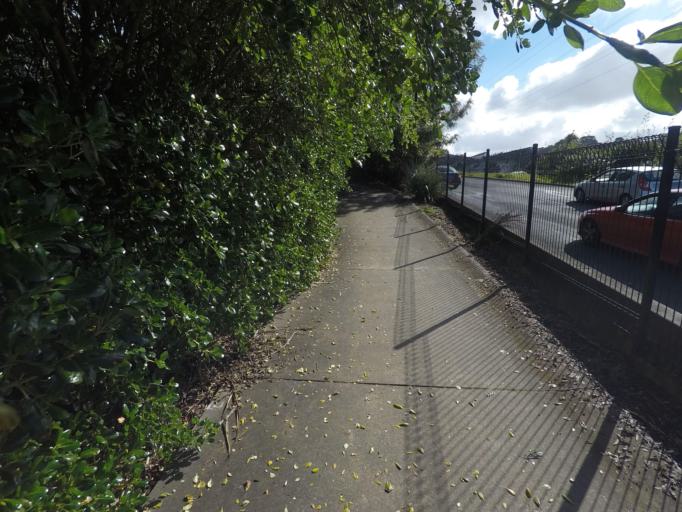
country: NZ
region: Auckland
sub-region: Auckland
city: Mangere
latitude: -36.9224
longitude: 174.7679
